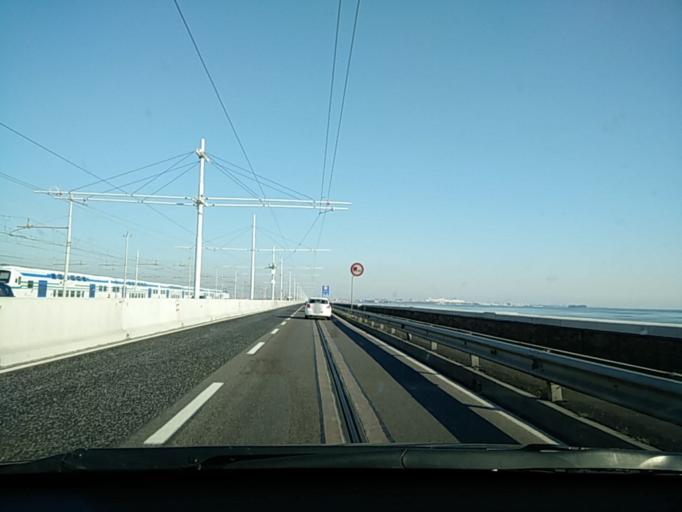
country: IT
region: Veneto
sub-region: Provincia di Venezia
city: Campalto
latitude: 45.4640
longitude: 12.2805
